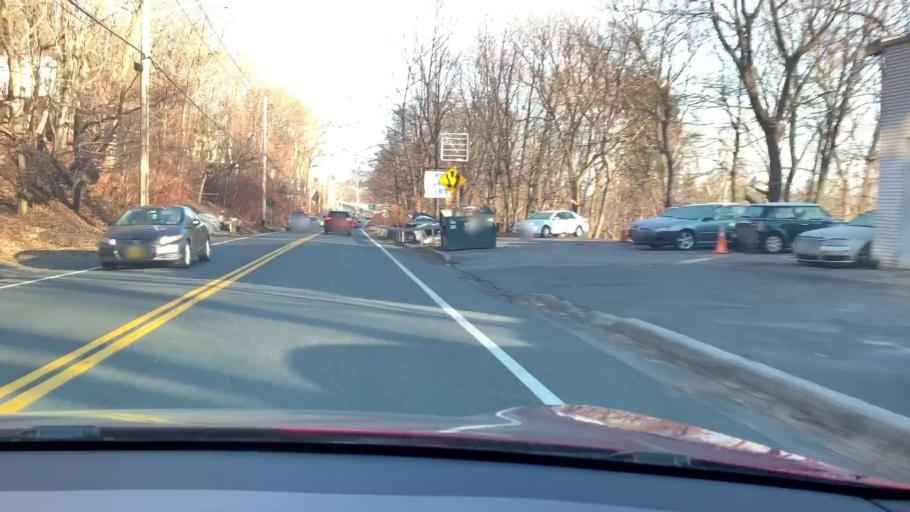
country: US
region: New York
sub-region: Rockland County
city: South Nyack
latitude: 41.0759
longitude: -73.9231
